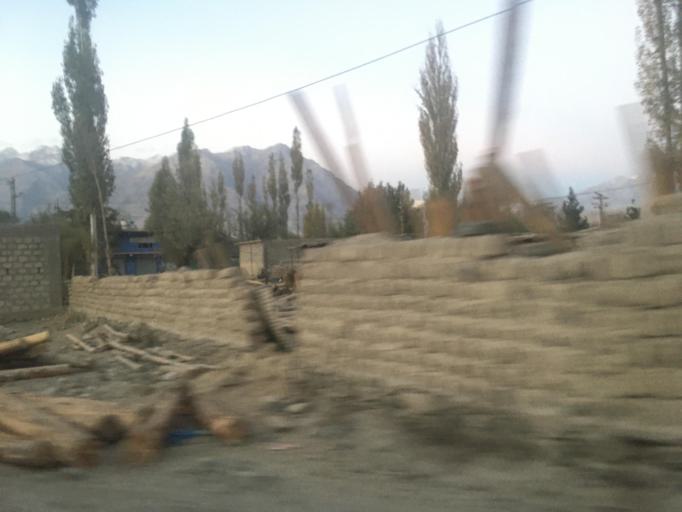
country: PK
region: Gilgit-Baltistan
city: Skardu
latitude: 35.2945
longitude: 75.5702
